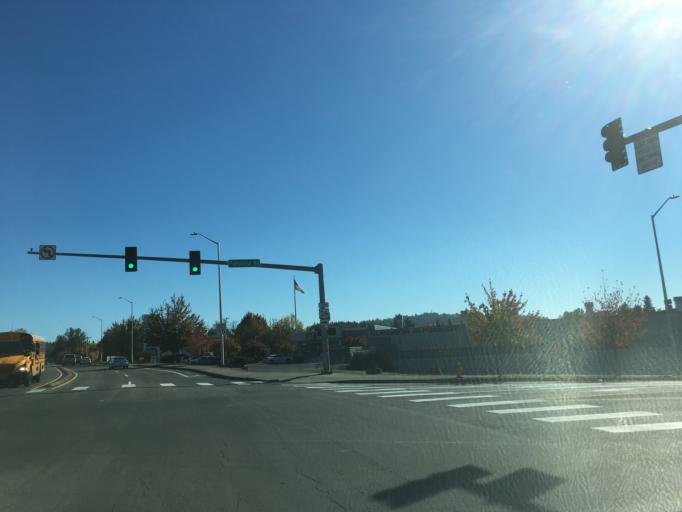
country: US
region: Oregon
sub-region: Multnomah County
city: Gresham
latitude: 45.4872
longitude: -122.3983
